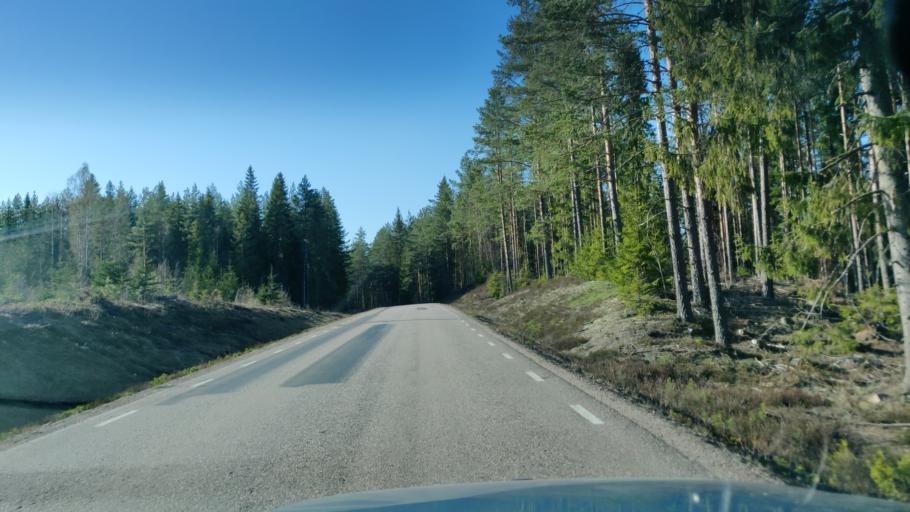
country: SE
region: Vaermland
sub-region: Sunne Kommun
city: Sunne
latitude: 59.9907
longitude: 13.3094
